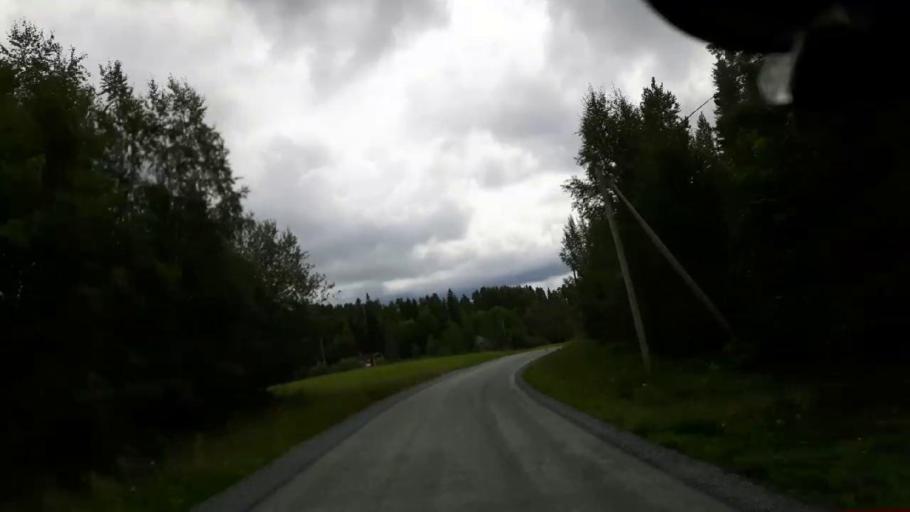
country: SE
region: Jaemtland
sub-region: Krokoms Kommun
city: Krokom
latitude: 63.5730
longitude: 14.2396
